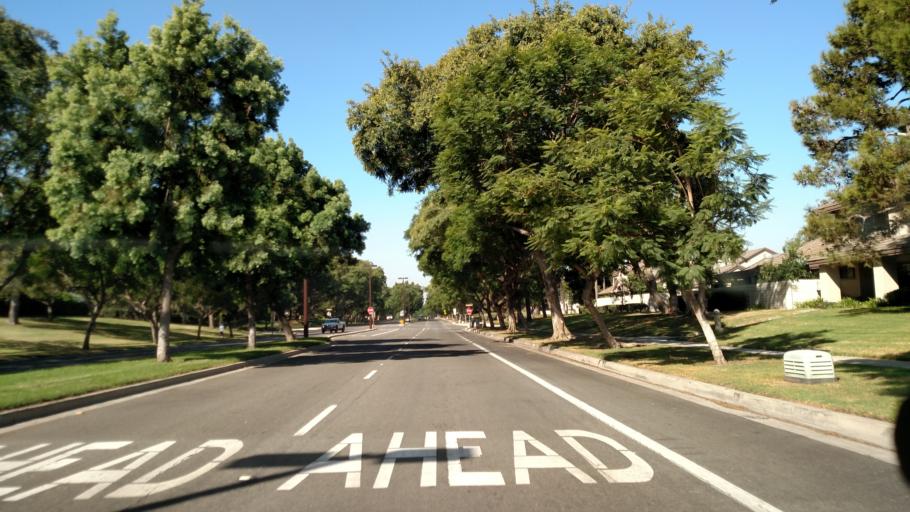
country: US
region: California
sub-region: Orange County
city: Irvine
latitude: 33.6671
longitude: -117.8008
